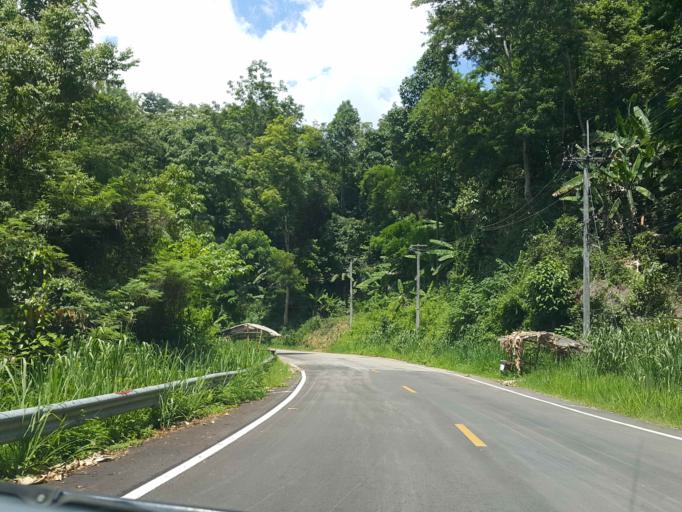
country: TH
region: Chiang Mai
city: Samoeng
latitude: 18.8538
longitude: 98.7779
